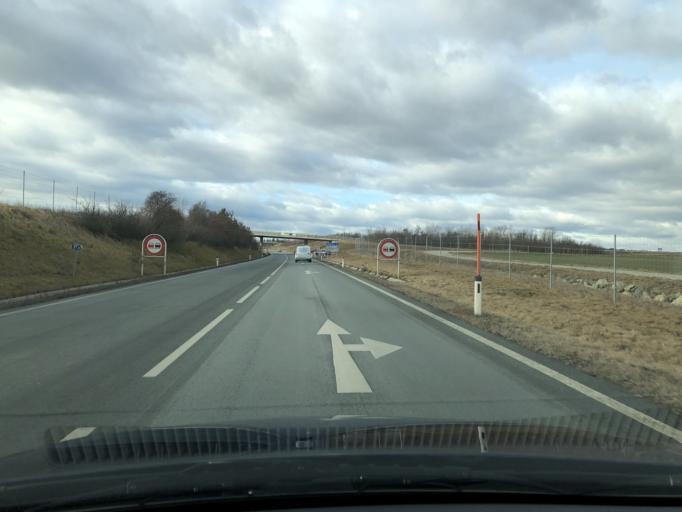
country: AT
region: Burgenland
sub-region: Politischer Bezirk Oberwart
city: Markt Neuhodis
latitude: 47.2744
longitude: 16.3936
